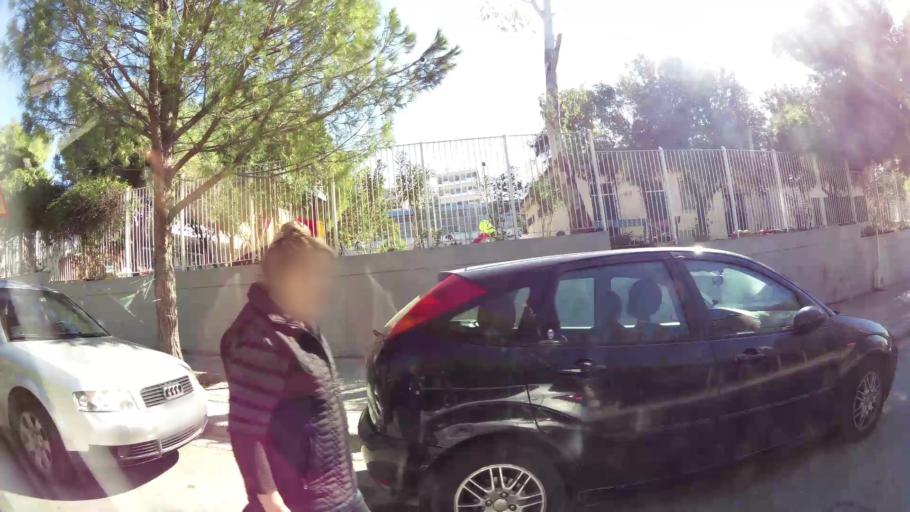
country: GR
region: Attica
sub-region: Nomarchia Athinas
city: Metamorfosi
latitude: 38.0645
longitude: 23.7669
